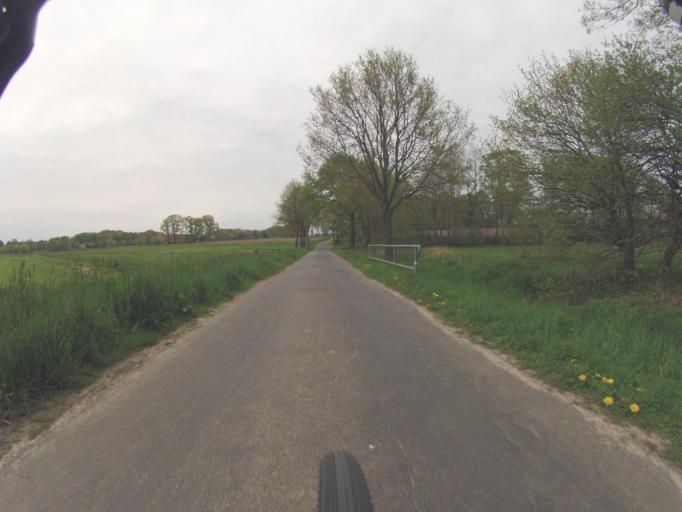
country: DE
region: North Rhine-Westphalia
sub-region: Regierungsbezirk Munster
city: Mettingen
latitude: 52.2944
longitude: 7.8323
